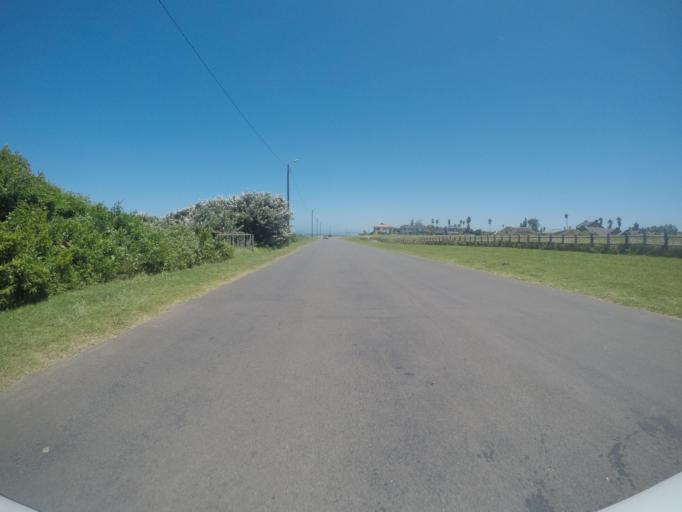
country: ZA
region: Eastern Cape
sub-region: Buffalo City Metropolitan Municipality
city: East London
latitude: -32.9525
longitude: 28.0129
